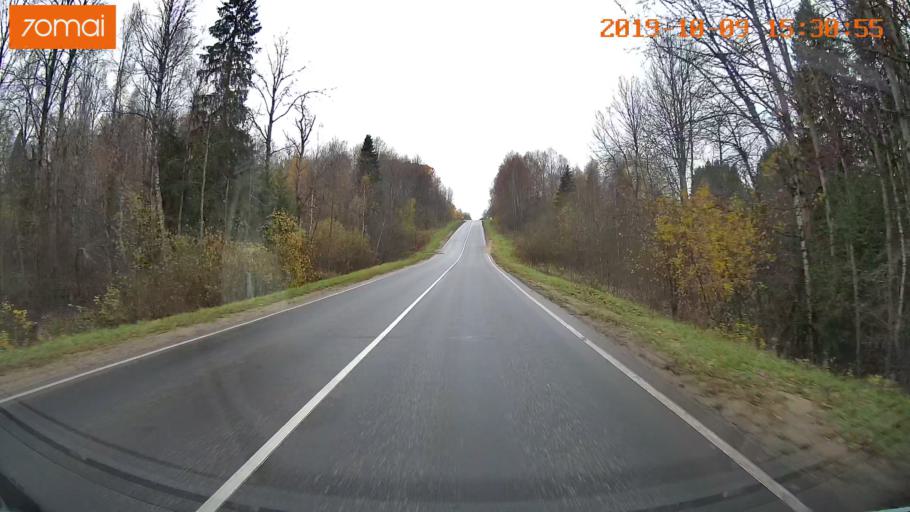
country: RU
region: Kostroma
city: Susanino
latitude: 57.9751
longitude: 41.3154
